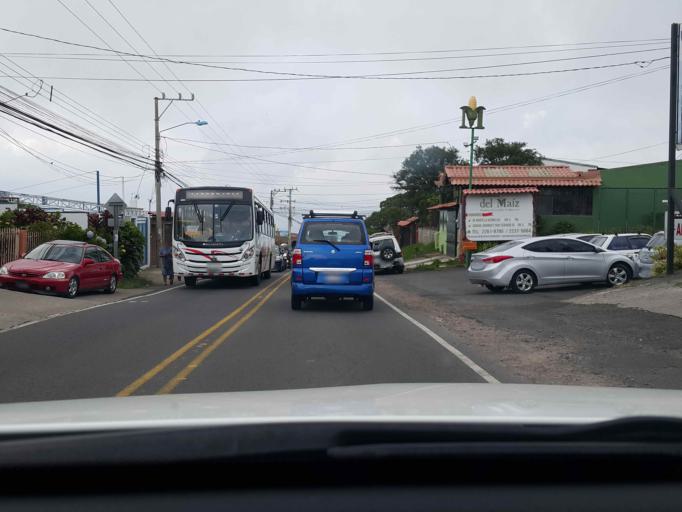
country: CR
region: Heredia
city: San Josecito
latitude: 10.0243
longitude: -84.0959
